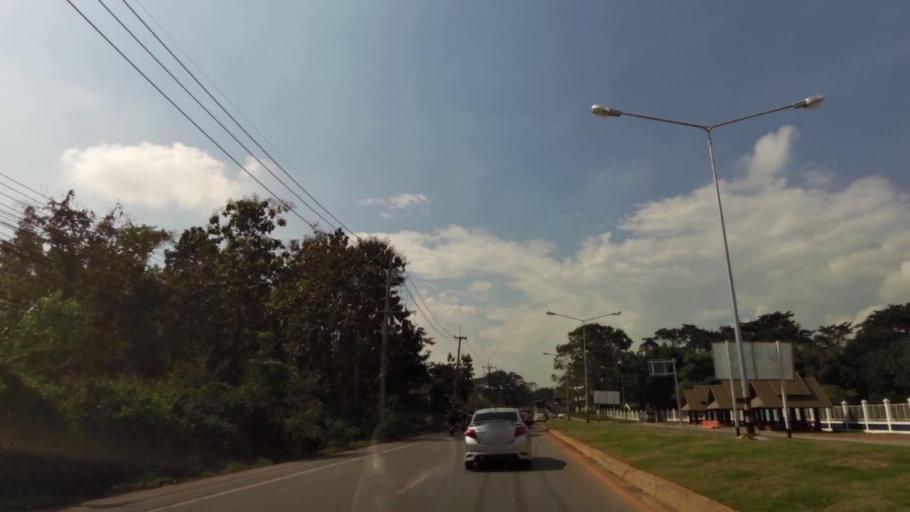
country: TH
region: Chiang Rai
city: Chiang Rai
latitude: 19.8755
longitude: 99.7846
